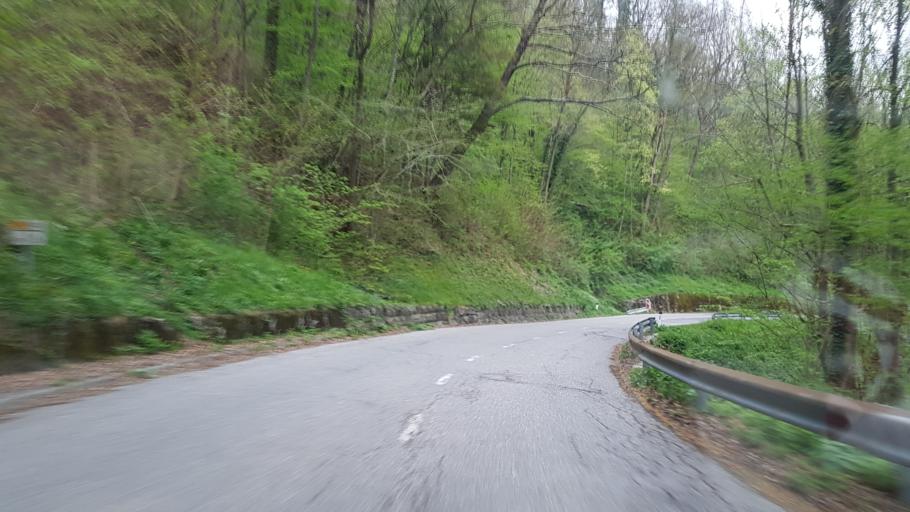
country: SI
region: Kobarid
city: Kobarid
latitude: 46.2525
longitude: 13.5115
